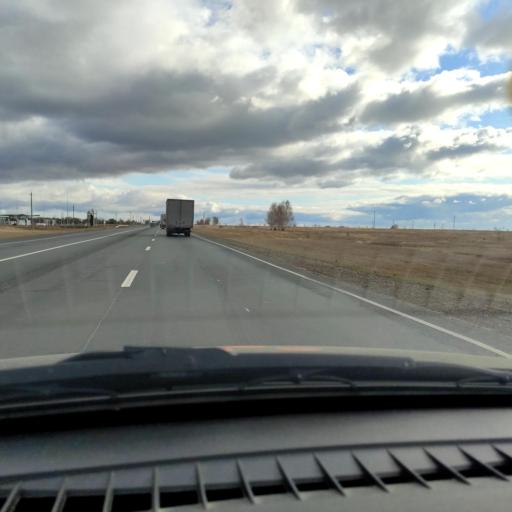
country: RU
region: Samara
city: Syzran'
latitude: 53.2103
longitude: 48.4929
